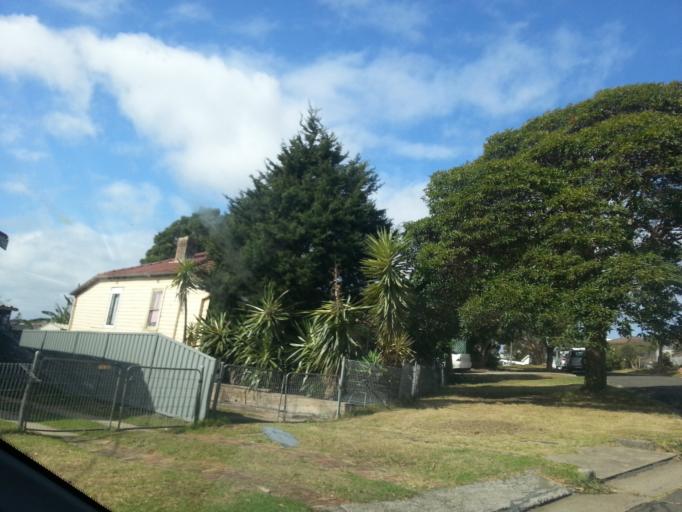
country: AU
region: New South Wales
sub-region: Wollongong
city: Port Kembla
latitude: -34.4824
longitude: 150.8987
